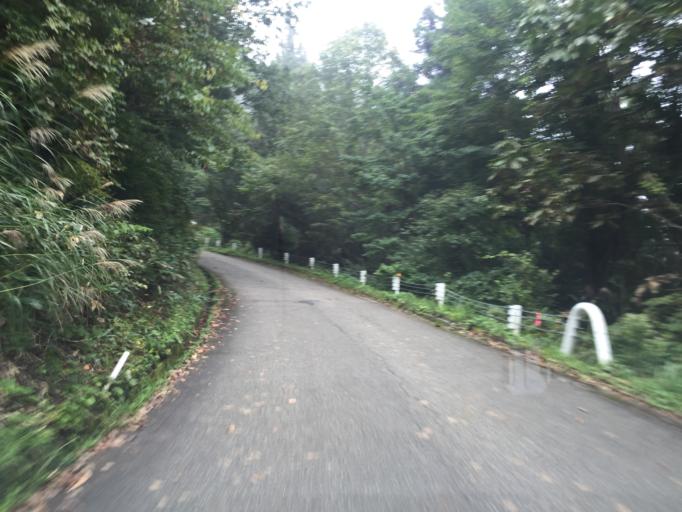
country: JP
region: Fukushima
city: Inawashiro
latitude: 37.4859
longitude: 139.9710
